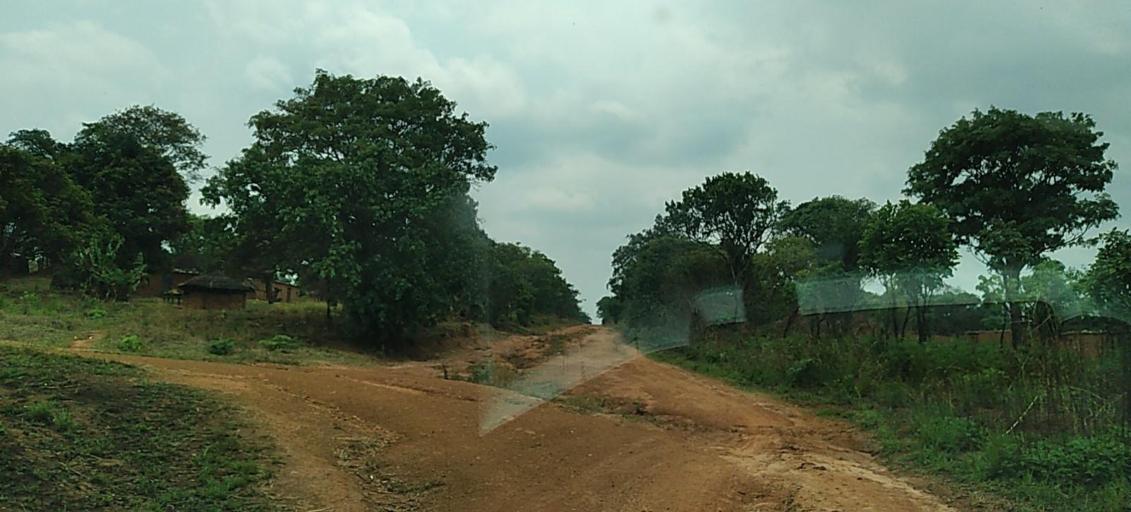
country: ZM
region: North-Western
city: Mwinilunga
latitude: -11.5356
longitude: 24.7834
